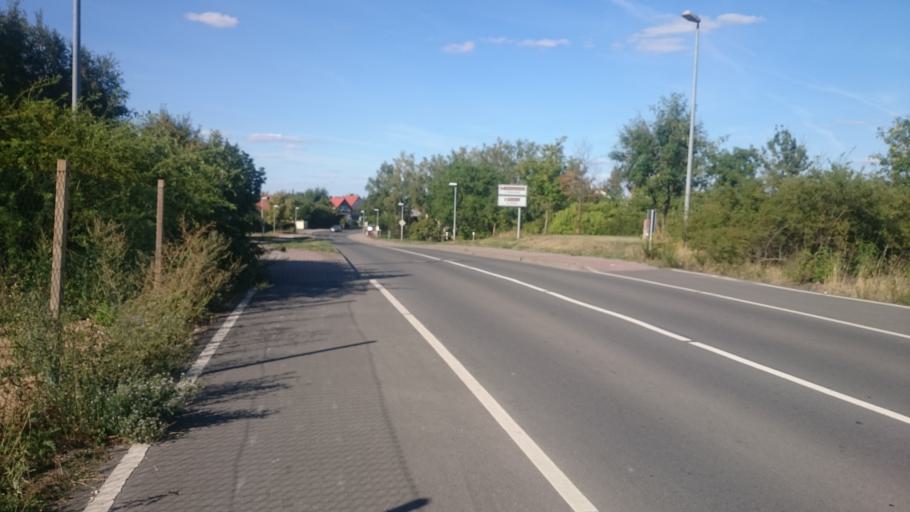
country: DE
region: Saxony-Anhalt
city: Gernrode
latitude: 51.7302
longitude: 11.1510
